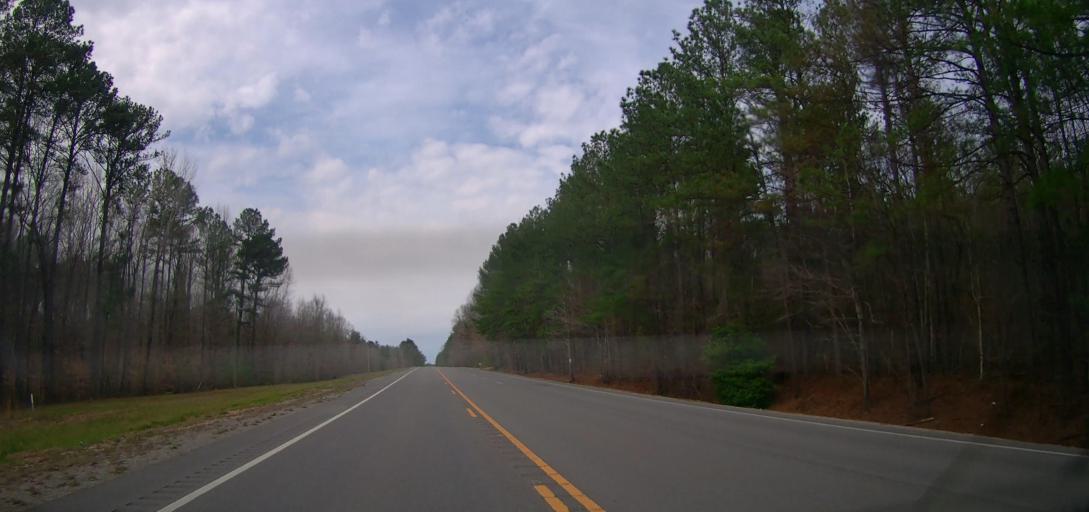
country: US
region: Alabama
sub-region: Marion County
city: Guin
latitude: 34.0136
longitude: -87.9361
